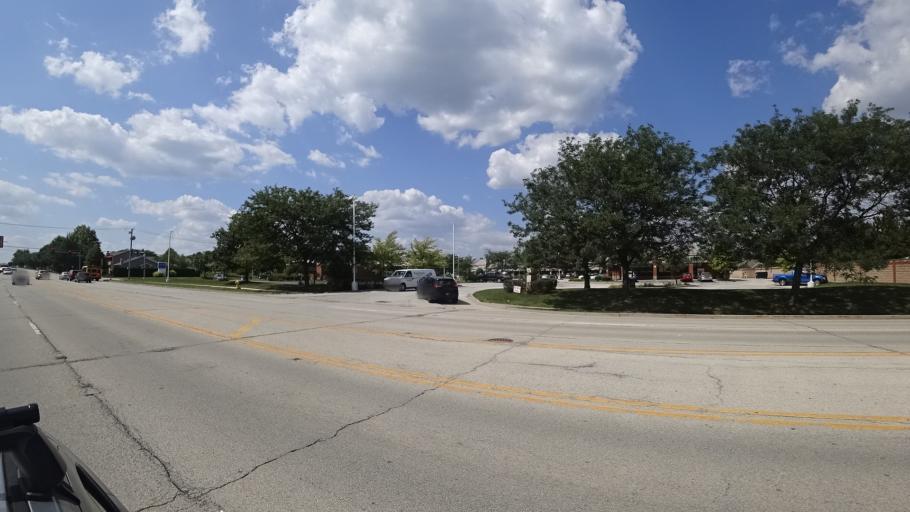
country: US
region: Illinois
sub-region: Cook County
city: Orland Park
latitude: 41.6311
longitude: -87.8185
